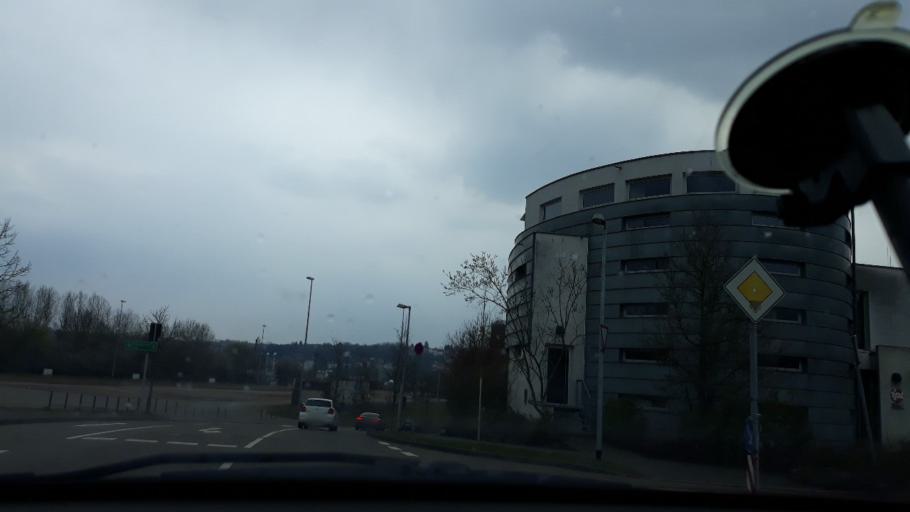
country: DE
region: Saarland
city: Saarbrucken
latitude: 49.2400
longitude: 6.9603
